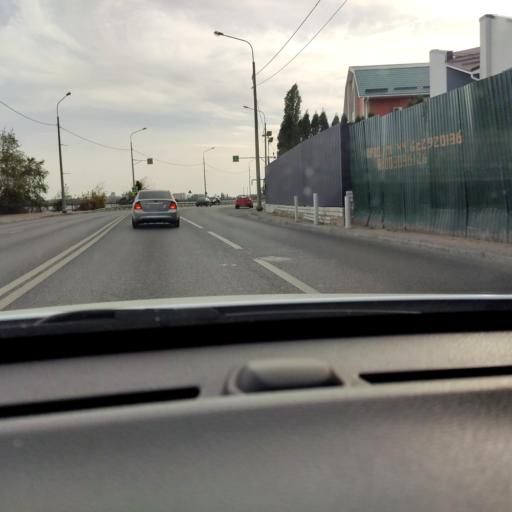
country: RU
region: Voronezj
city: Voronezh
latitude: 51.6850
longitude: 39.2287
